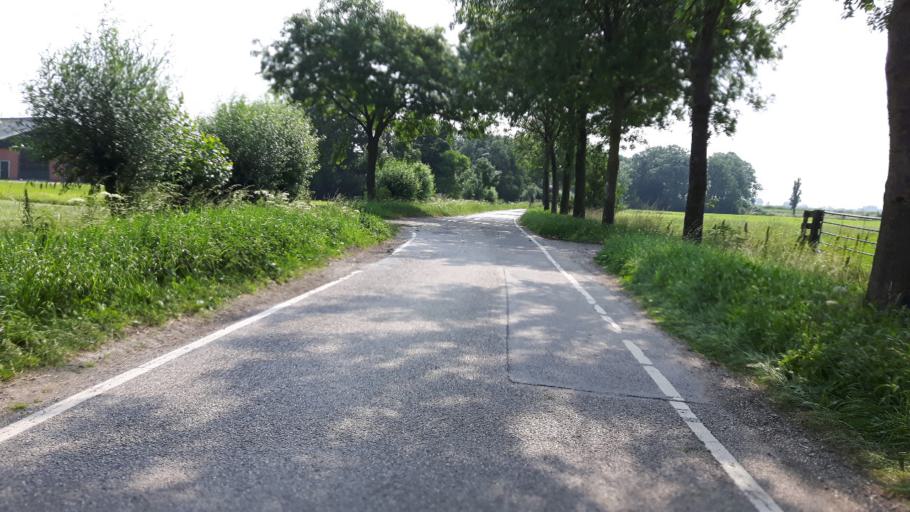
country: NL
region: Utrecht
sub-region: Gemeente Montfoort
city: Montfoort
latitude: 52.0702
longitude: 4.9272
